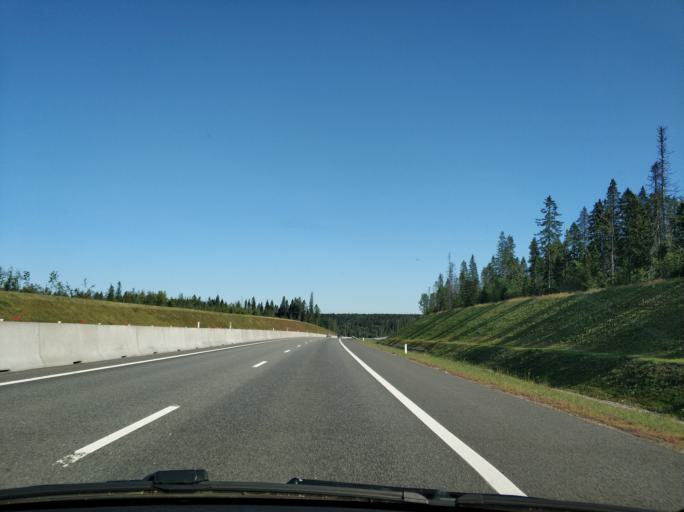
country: RU
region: Leningrad
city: Sosnovo
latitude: 60.4505
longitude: 30.2000
